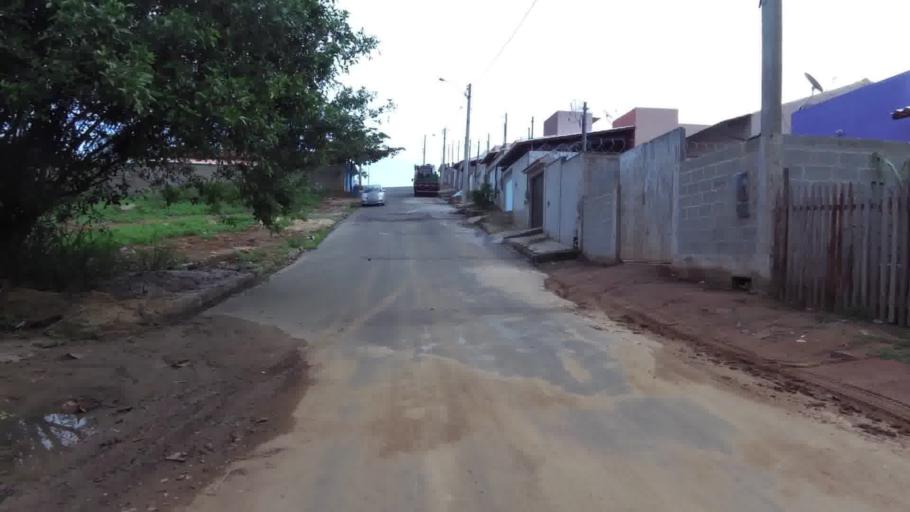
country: BR
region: Espirito Santo
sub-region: Piuma
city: Piuma
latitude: -20.7956
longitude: -40.6429
